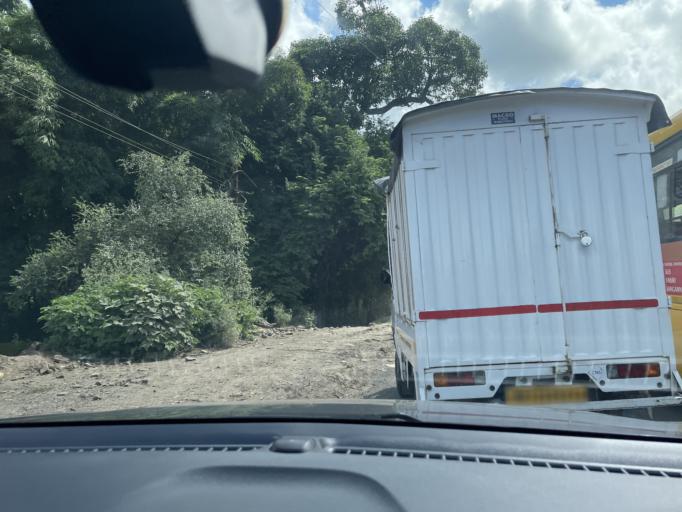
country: IN
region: Maharashtra
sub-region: Pune Division
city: Shivaji Nagar
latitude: 18.5248
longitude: 73.7721
